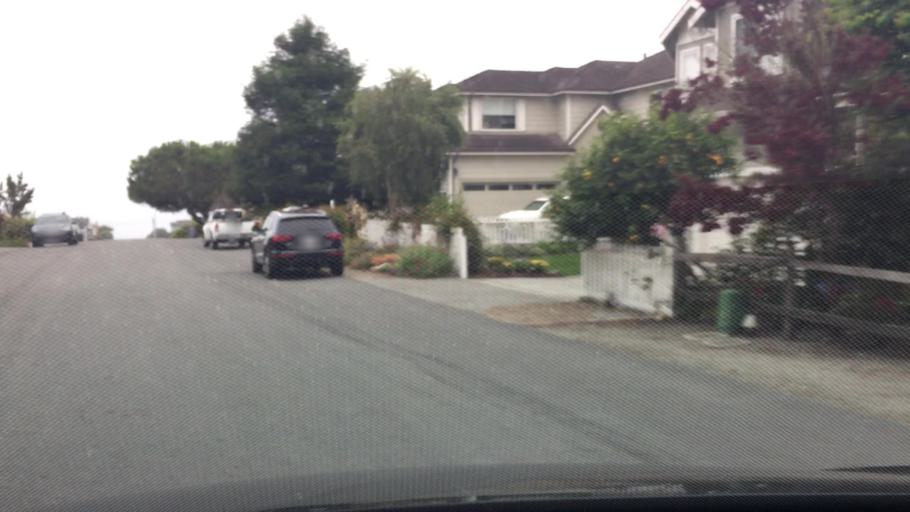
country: US
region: California
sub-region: San Mateo County
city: El Granada
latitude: 37.4981
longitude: -122.4586
